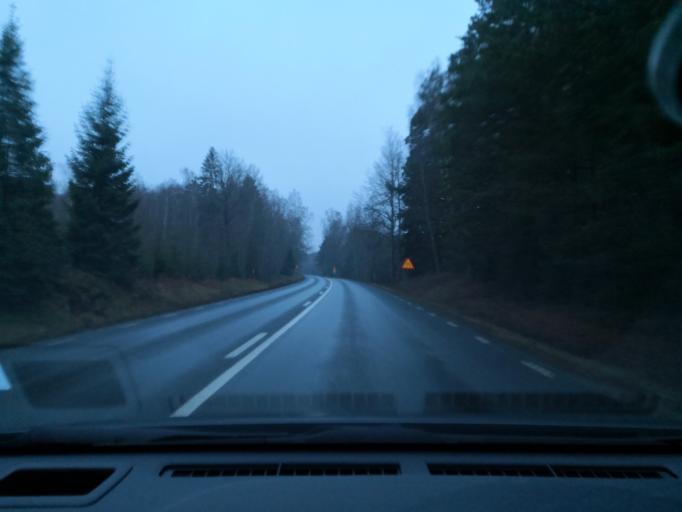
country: SE
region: Soedermanland
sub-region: Eskilstuna Kommun
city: Skogstorp
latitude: 59.2651
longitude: 16.3716
